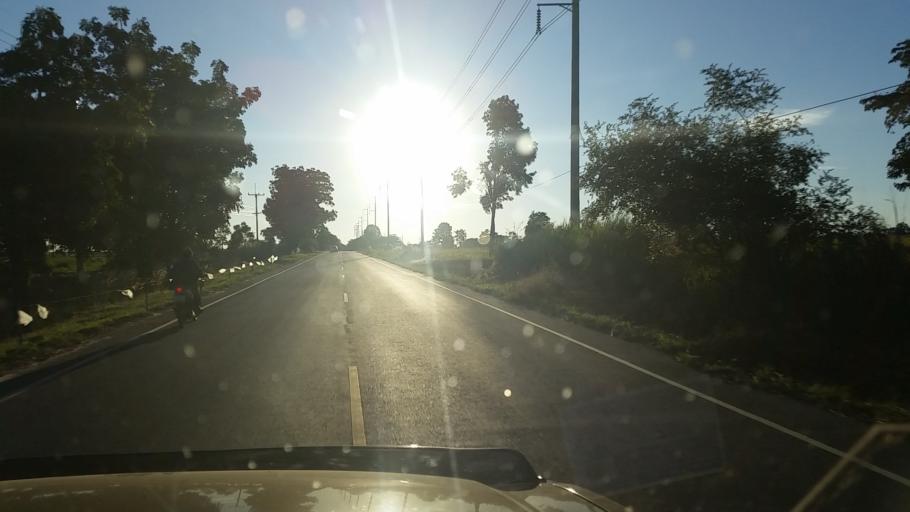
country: TH
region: Chaiyaphum
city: Sap Yai
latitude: 15.6613
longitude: 101.6612
